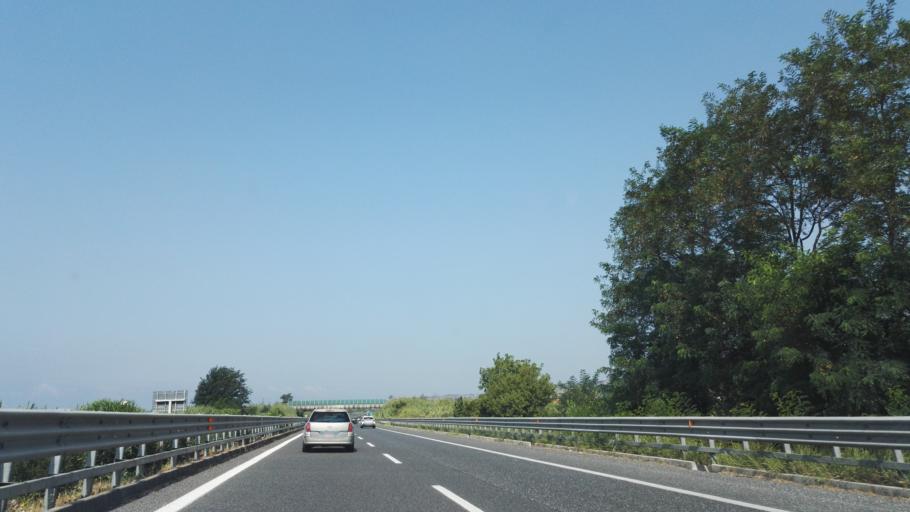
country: IT
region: Calabria
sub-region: Provincia di Catanzaro
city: Santa Eufemia Lamezia
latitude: 38.9311
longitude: 16.2302
